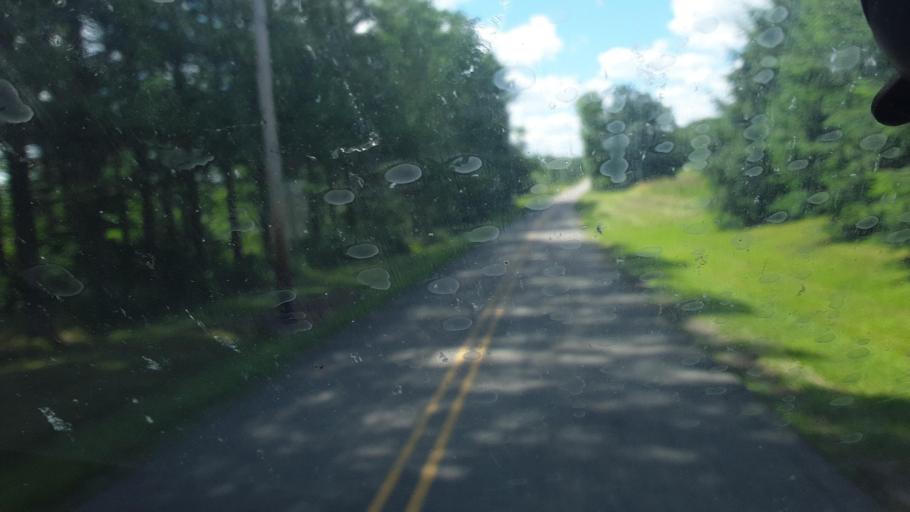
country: US
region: Pennsylvania
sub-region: Lawrence County
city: New Castle
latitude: 41.0414
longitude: -80.2145
